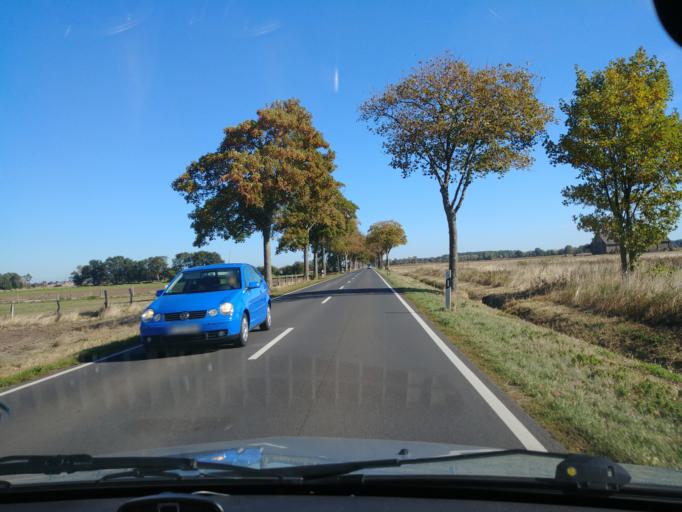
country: DE
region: Lower Saxony
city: Hillerse
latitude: 52.4177
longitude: 10.4128
